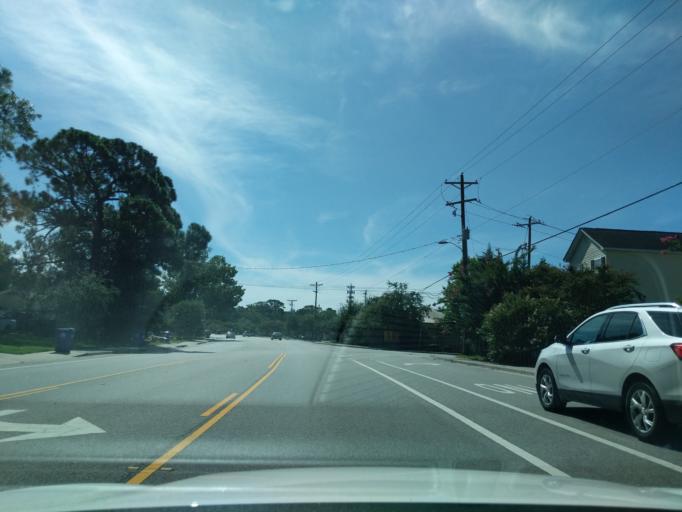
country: US
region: South Carolina
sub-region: Charleston County
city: Charleston
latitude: 32.7431
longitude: -79.9379
